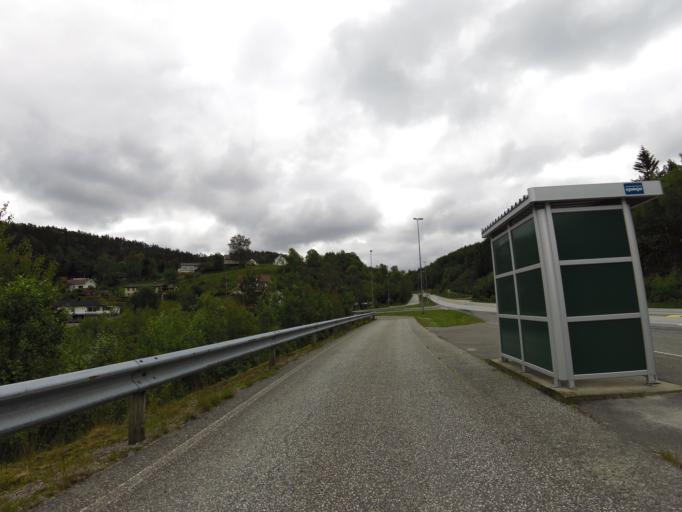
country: NO
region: Vest-Agder
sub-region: Flekkefjord
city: Flekkefjord
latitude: 58.2951
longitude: 6.6893
